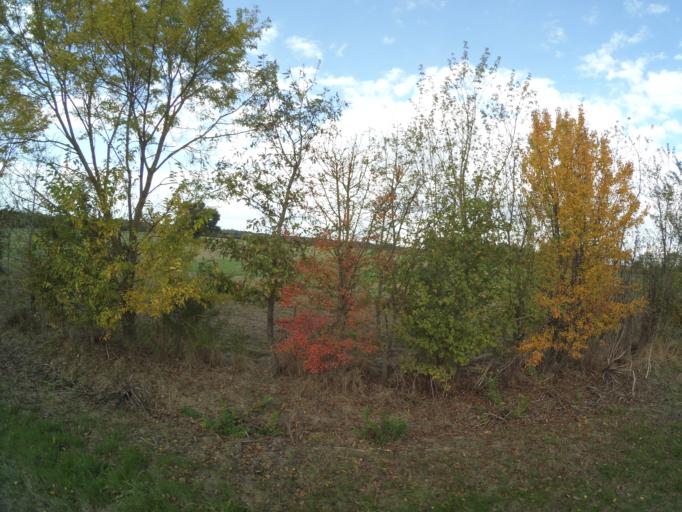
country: FR
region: Pays de la Loire
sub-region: Departement de la Loire-Atlantique
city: Saint-Lumine-de-Clisson
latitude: 47.0707
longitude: -1.3323
